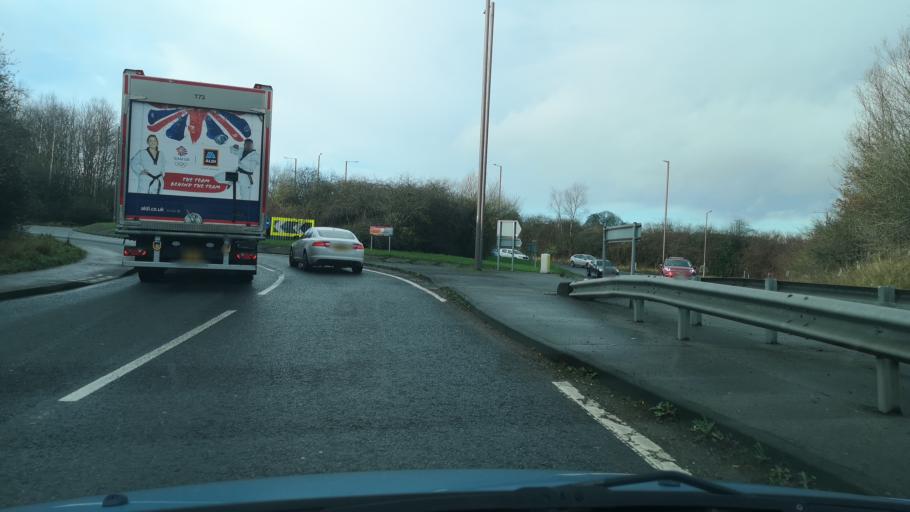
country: GB
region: England
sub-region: Barnsley
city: Hoyland Nether
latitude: 53.5112
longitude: -1.4338
